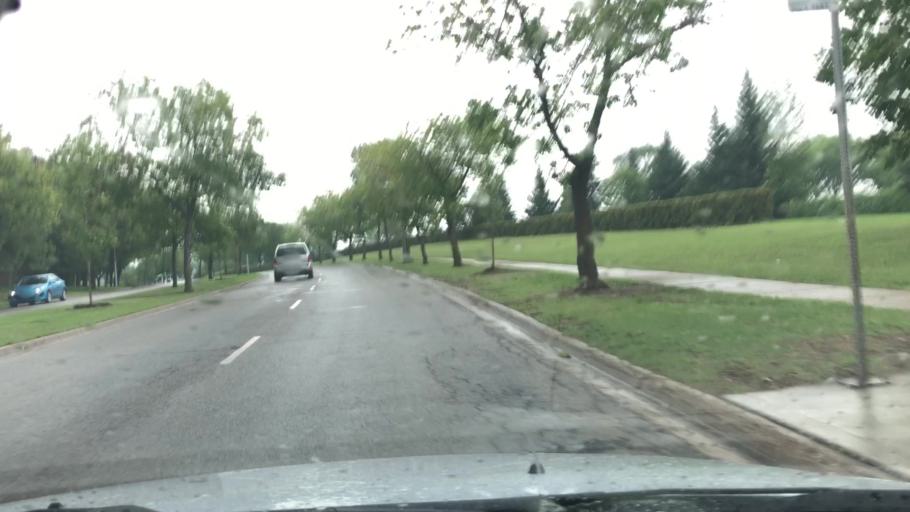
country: CA
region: Alberta
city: St. Albert
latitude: 53.6410
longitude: -113.6334
